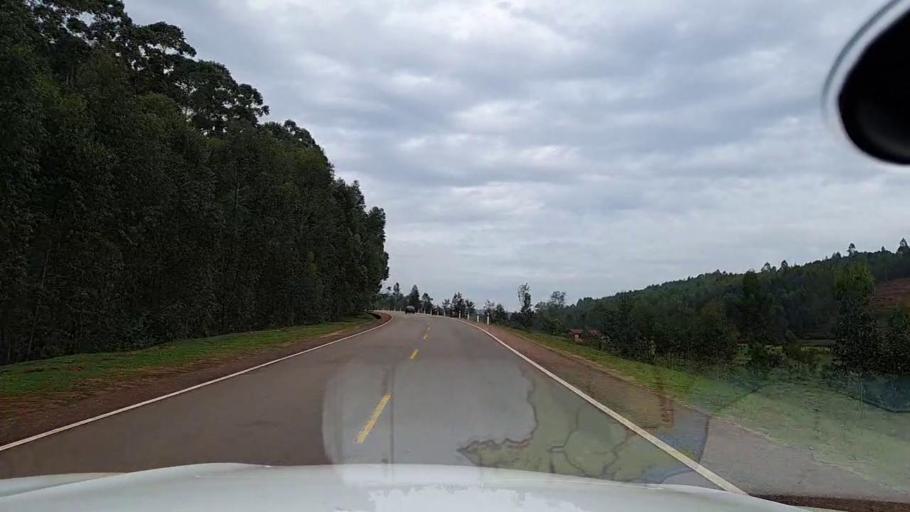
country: RW
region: Southern Province
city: Butare
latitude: -2.5636
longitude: 29.7231
